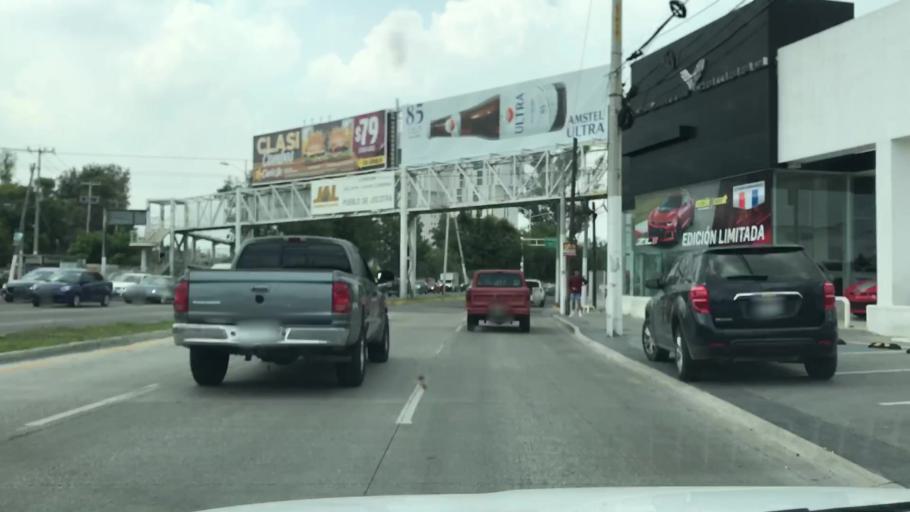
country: MX
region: Jalisco
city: Guadalajara
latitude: 20.6829
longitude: -103.4391
